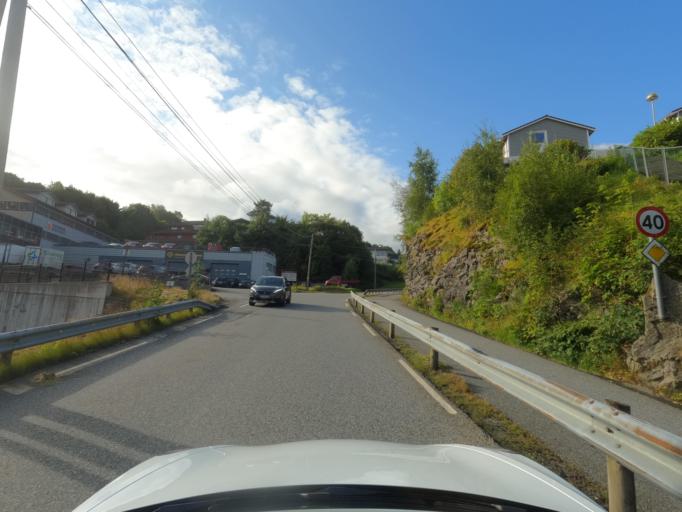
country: NO
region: Hordaland
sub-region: Bergen
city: Sandsli
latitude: 60.2954
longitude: 5.3440
